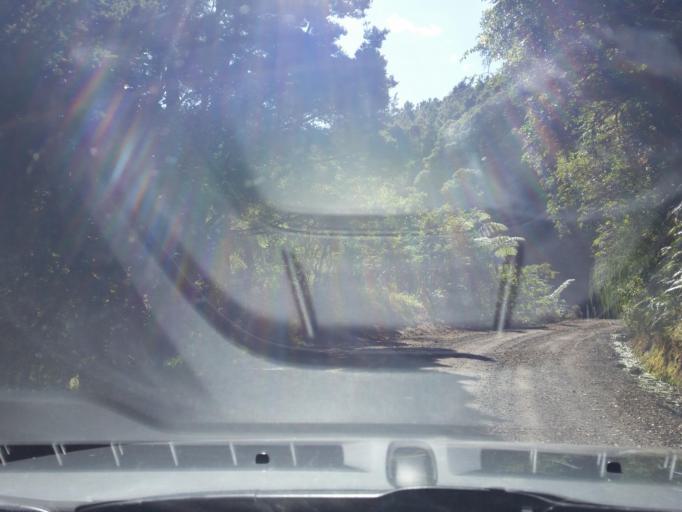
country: NZ
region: Northland
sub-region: Kaipara District
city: Dargaville
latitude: -35.7077
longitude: 173.6244
